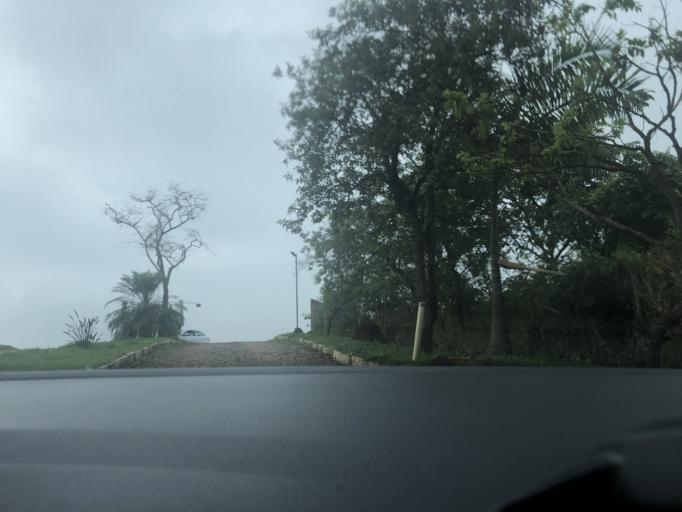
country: BR
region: Minas Gerais
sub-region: Congonhas
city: Congonhas
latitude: -20.6125
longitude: -43.9178
